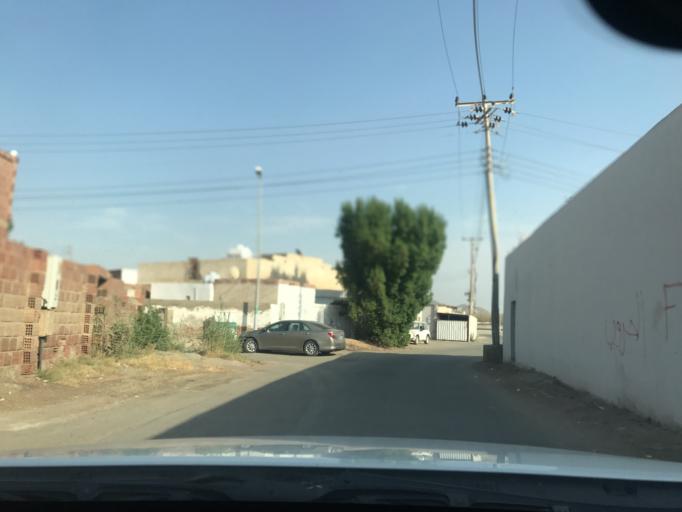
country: SA
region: Makkah
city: Al Jumum
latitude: 21.4430
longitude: 39.5351
